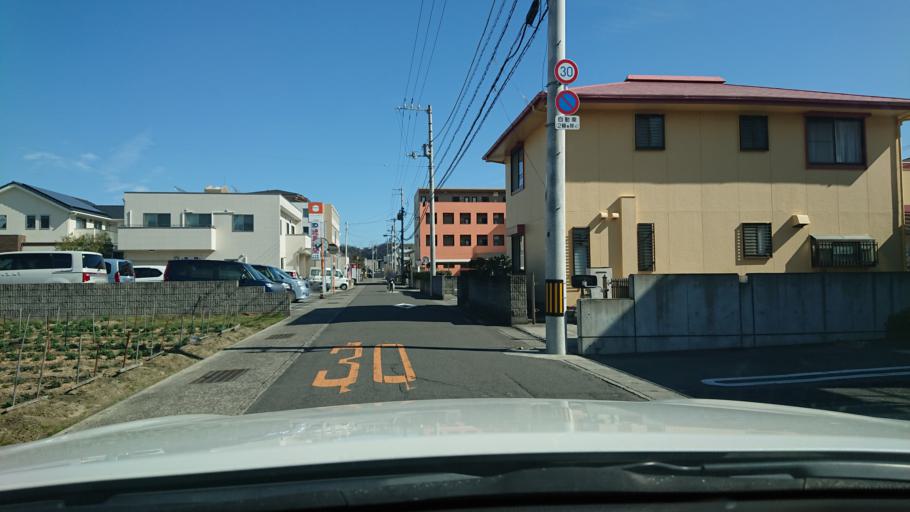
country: JP
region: Tokushima
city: Tokushima-shi
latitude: 34.0511
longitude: 134.5559
